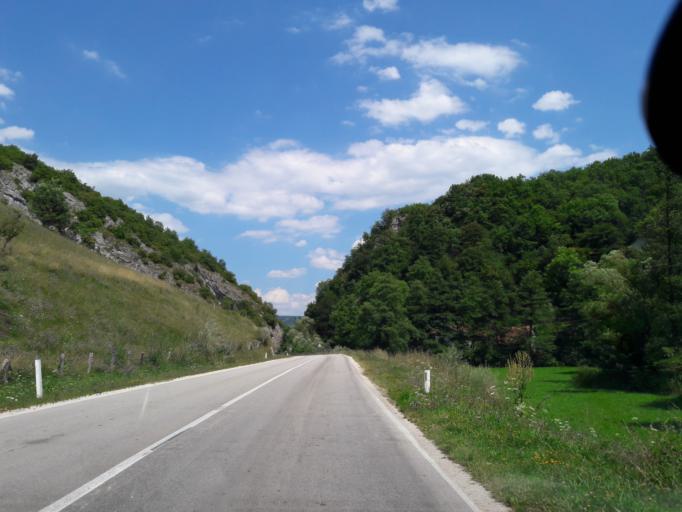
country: BA
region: Republika Srpska
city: Mrkonjic Grad
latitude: 44.4233
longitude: 17.1221
